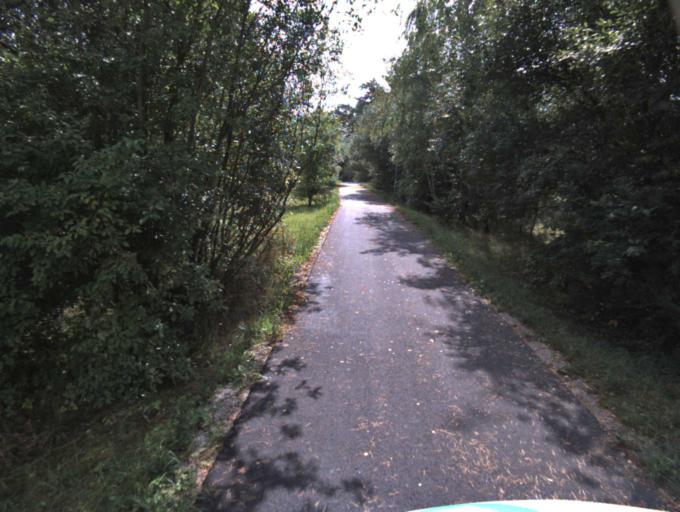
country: SE
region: Skane
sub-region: Kavlinge Kommun
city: Kaevlinge
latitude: 55.7823
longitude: 13.1107
